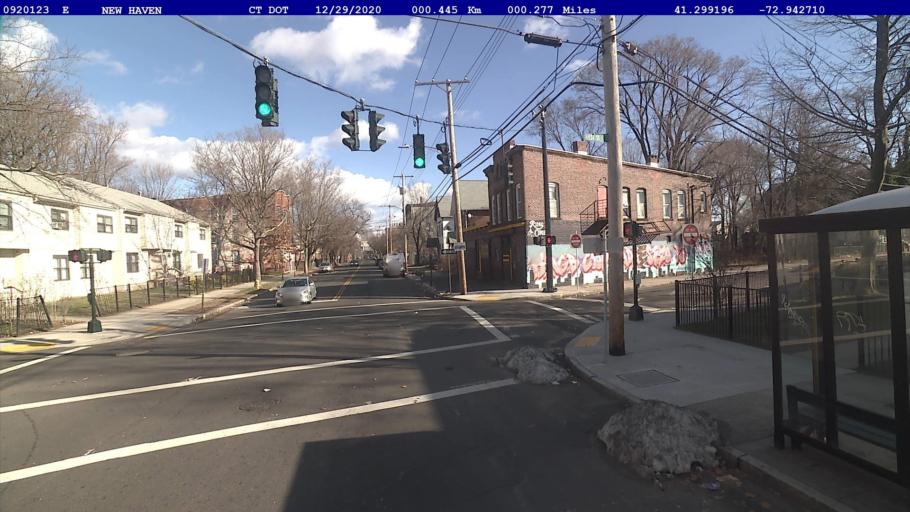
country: US
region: Connecticut
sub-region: New Haven County
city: New Haven
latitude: 41.2992
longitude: -72.9427
